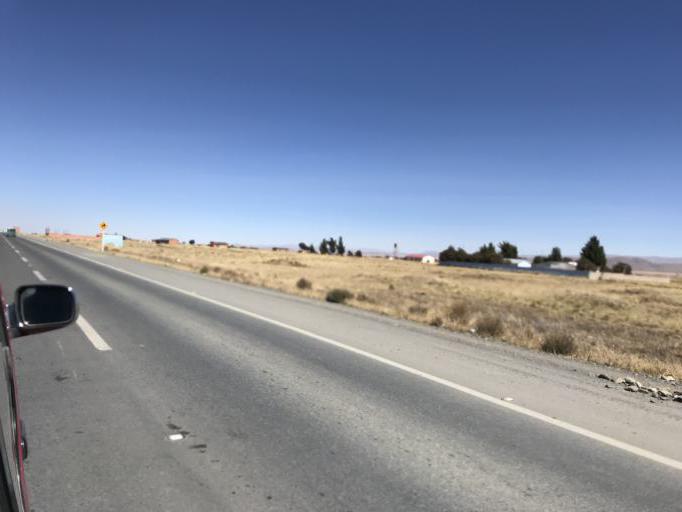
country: BO
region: La Paz
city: Batallas
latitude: -16.3482
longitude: -68.4047
